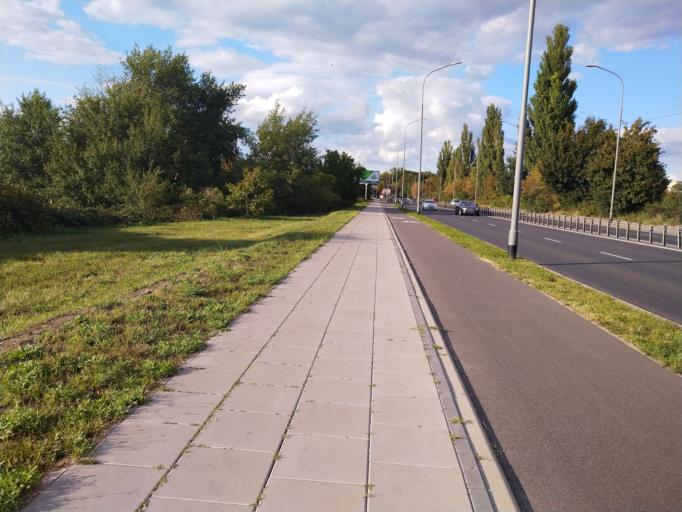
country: PL
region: West Pomeranian Voivodeship
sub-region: Szczecin
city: Szczecin
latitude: 53.4438
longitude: 14.5643
